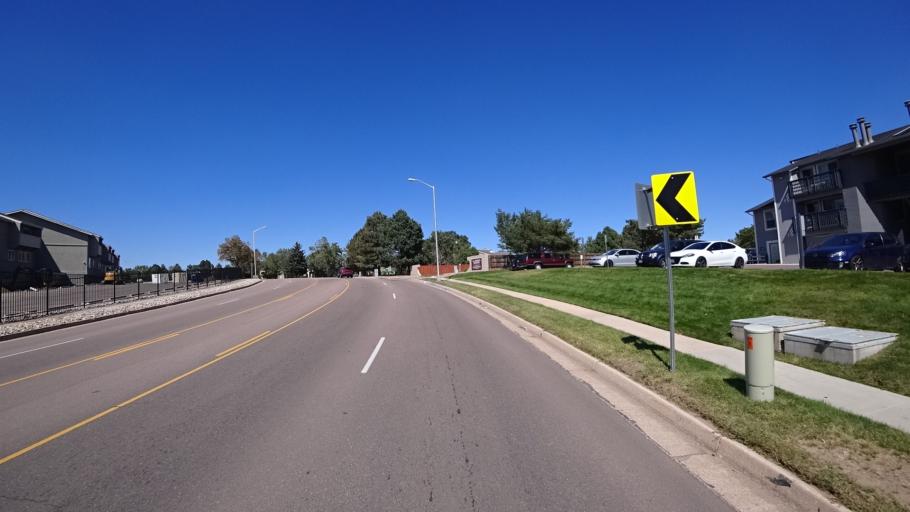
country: US
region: Colorado
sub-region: El Paso County
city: Cimarron Hills
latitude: 38.8351
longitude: -104.7453
